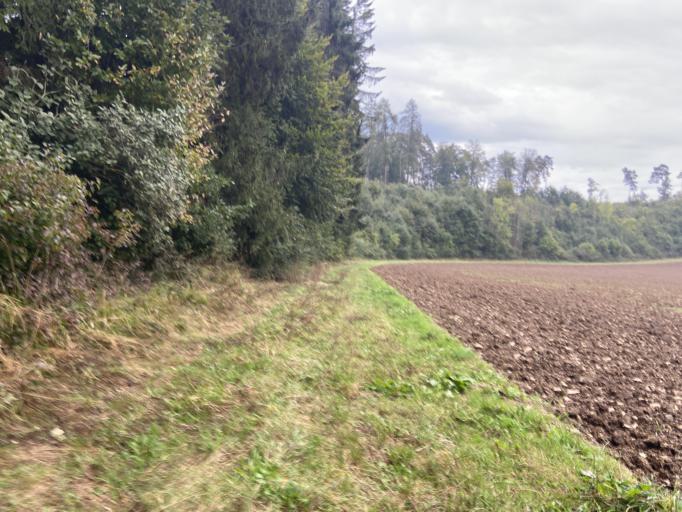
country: DE
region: Baden-Wuerttemberg
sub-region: Tuebingen Region
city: Bingen
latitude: 48.1173
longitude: 9.2489
